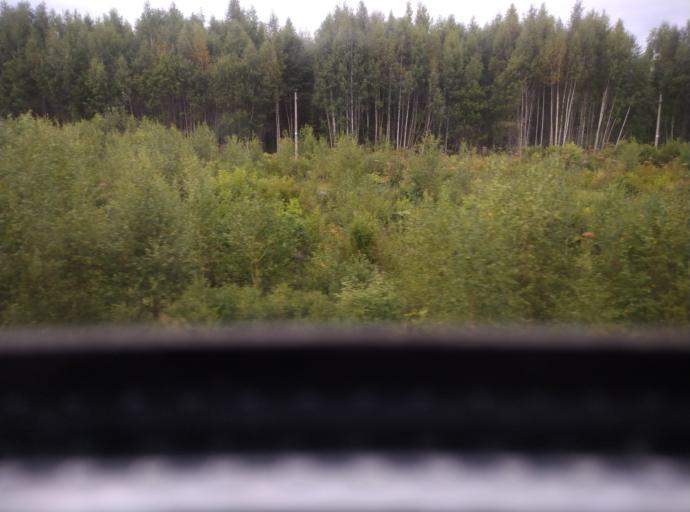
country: RU
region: Jaroslavl
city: Burmakino
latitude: 57.4398
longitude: 40.4012
